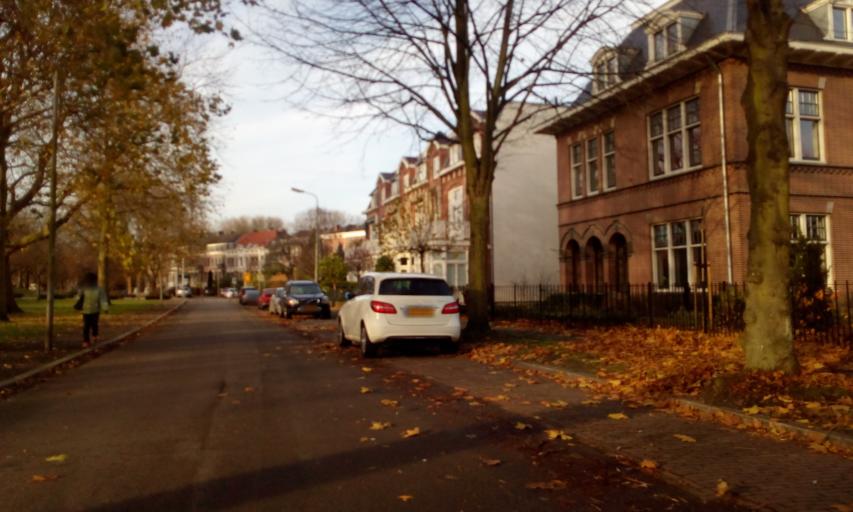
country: NL
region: South Holland
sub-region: Gemeente Delft
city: Delft
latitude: 52.0184
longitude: 4.3579
